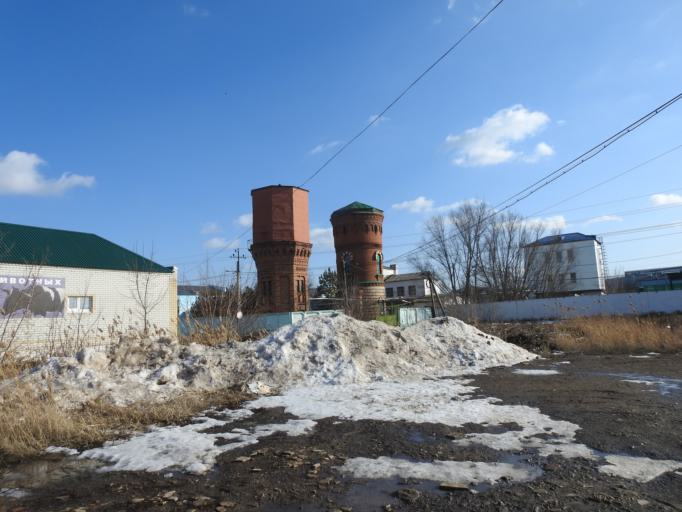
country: RU
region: Saratov
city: Yershov
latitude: 51.3489
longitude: 48.2751
